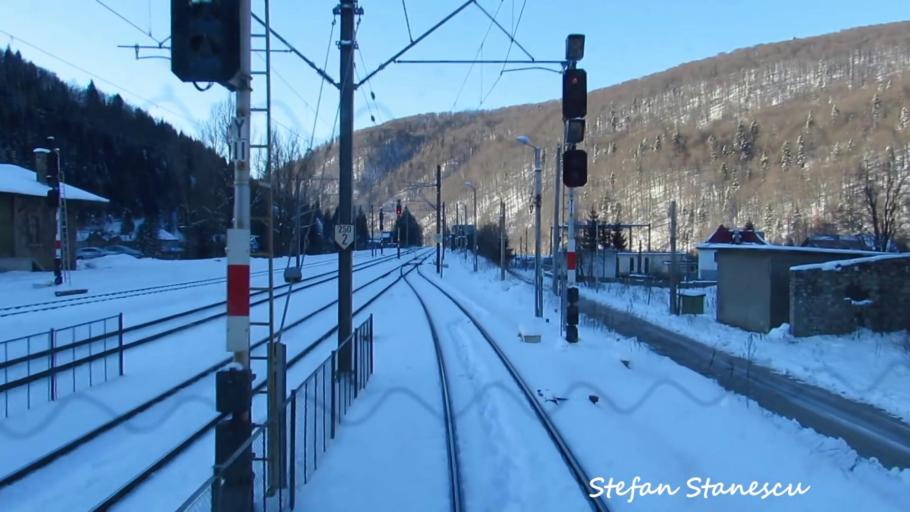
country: RO
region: Prahova
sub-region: Oras Azuga
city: Azuga
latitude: 45.4373
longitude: 25.5502
